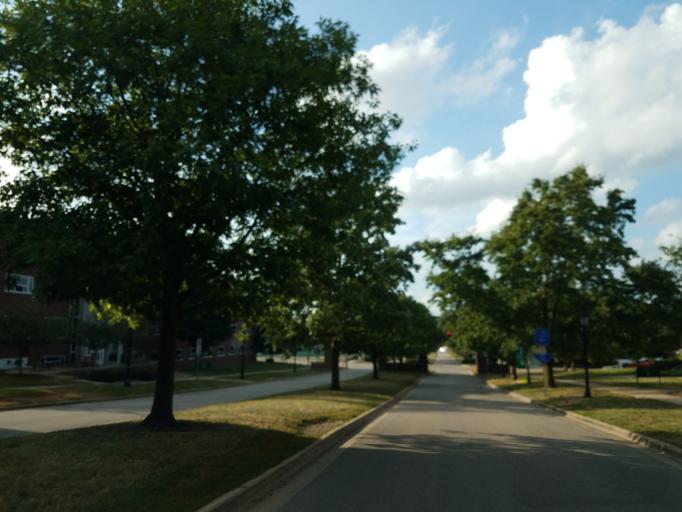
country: US
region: Illinois
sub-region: McLean County
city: Bloomington
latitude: 40.4922
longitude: -88.9908
